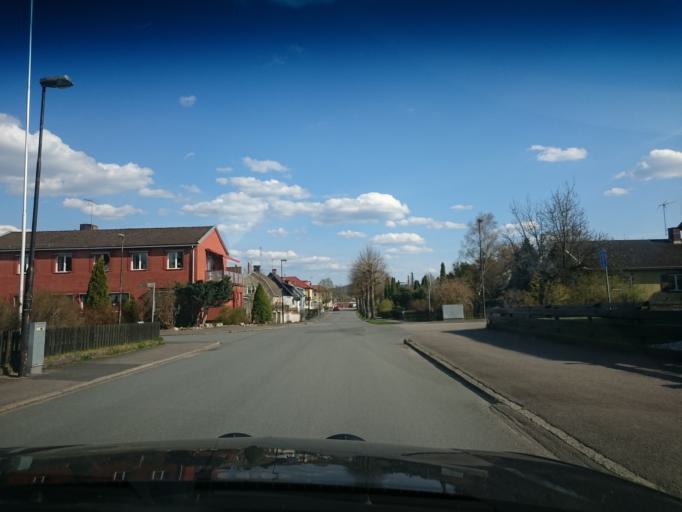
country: SE
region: Joenkoeping
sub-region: Vetlanda Kommun
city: Vetlanda
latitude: 57.4238
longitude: 15.0783
